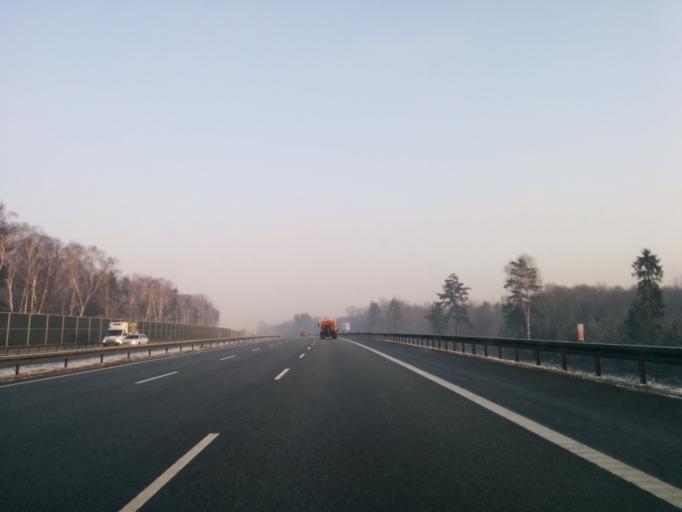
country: PL
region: Silesian Voivodeship
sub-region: Zabrze
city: Zabrze
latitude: 50.3234
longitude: 18.7286
